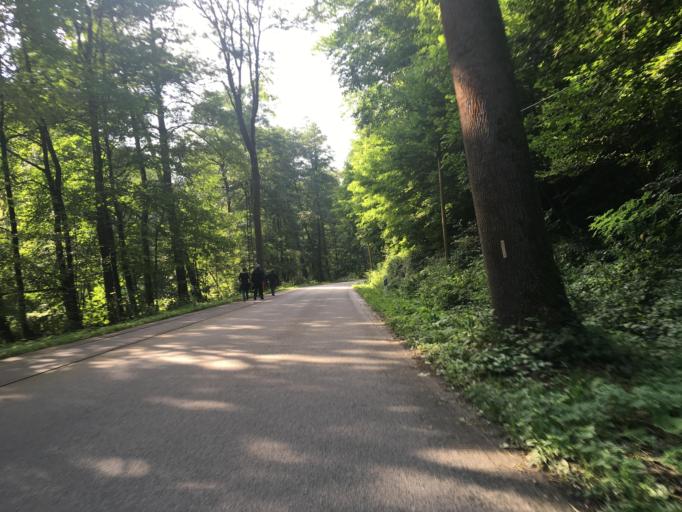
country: DE
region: Saxony
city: Bad Schandau
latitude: 50.9247
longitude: 14.1721
